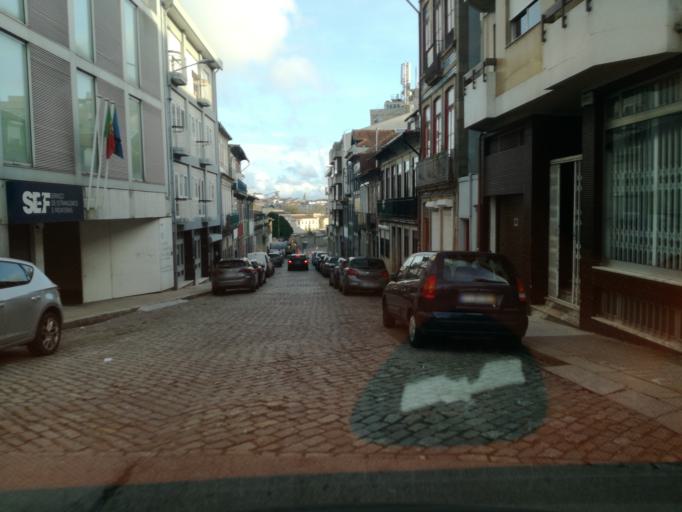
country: PT
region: Porto
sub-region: Porto
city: Porto
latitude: 41.1600
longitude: -8.6211
